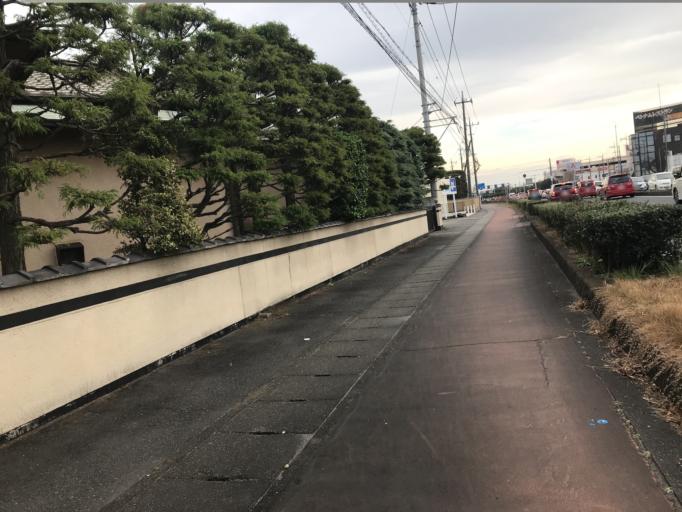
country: JP
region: Gunma
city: Ota
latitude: 36.2997
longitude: 139.3995
